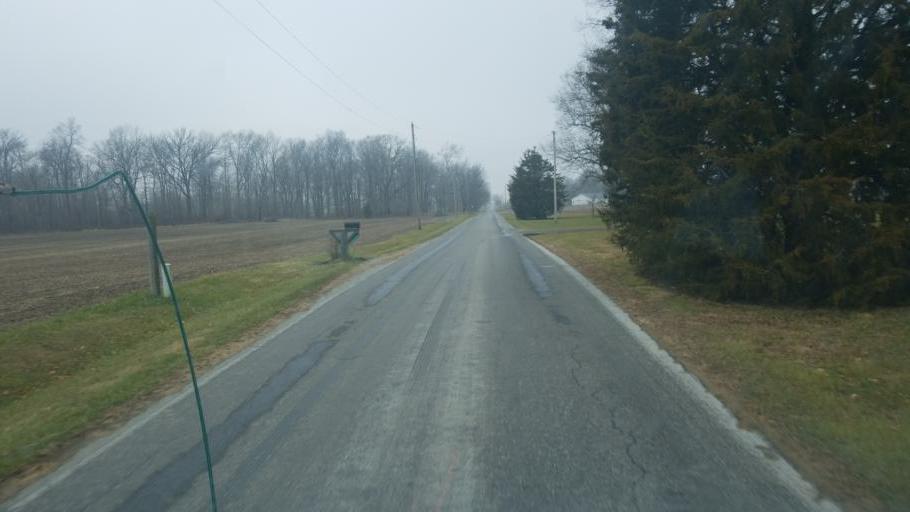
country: US
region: Ohio
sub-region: Hardin County
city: Kenton
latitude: 40.5963
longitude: -83.4804
